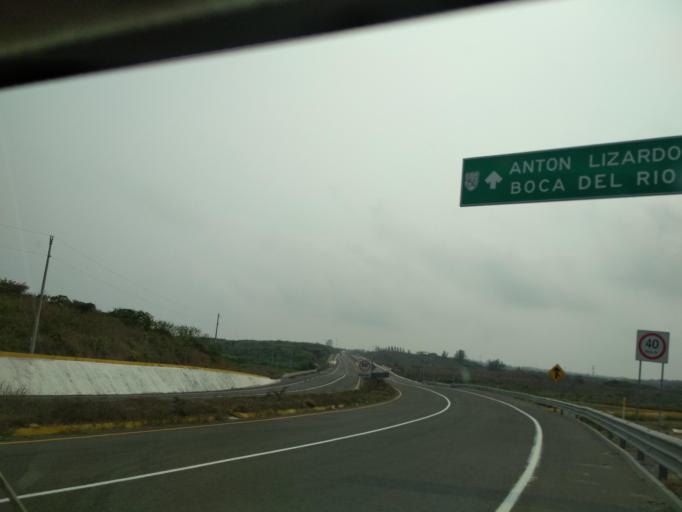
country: MX
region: Veracruz
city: Anton Lizardo
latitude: 19.0509
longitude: -96.0090
